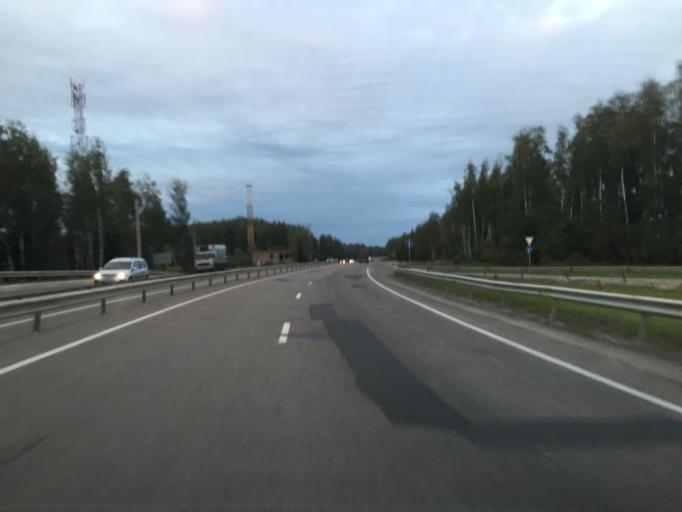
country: RU
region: Kaluga
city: Kaluga
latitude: 54.6286
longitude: 36.2896
